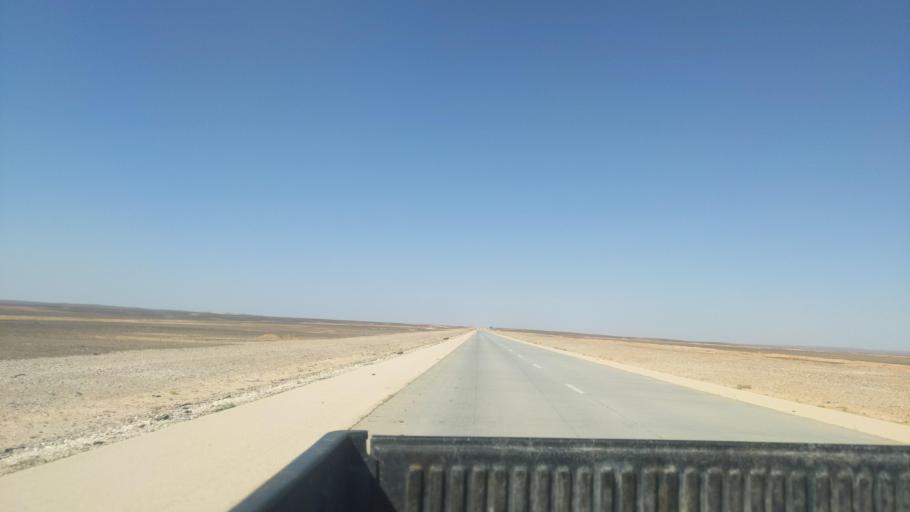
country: JO
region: Amman
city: Al Azraq ash Shamali
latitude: 31.4454
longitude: 36.7614
